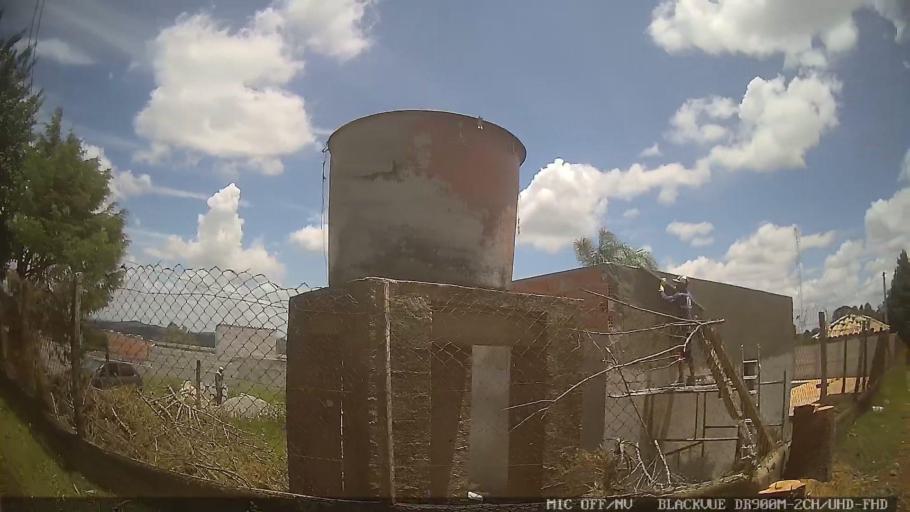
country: BR
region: Sao Paulo
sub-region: Atibaia
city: Atibaia
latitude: -23.0411
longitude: -46.5356
